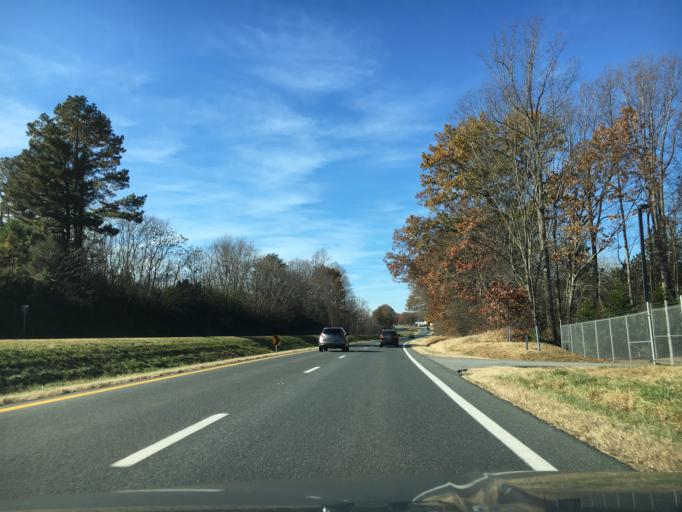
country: US
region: Virginia
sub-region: Campbell County
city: Concord
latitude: 37.3482
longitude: -78.9652
